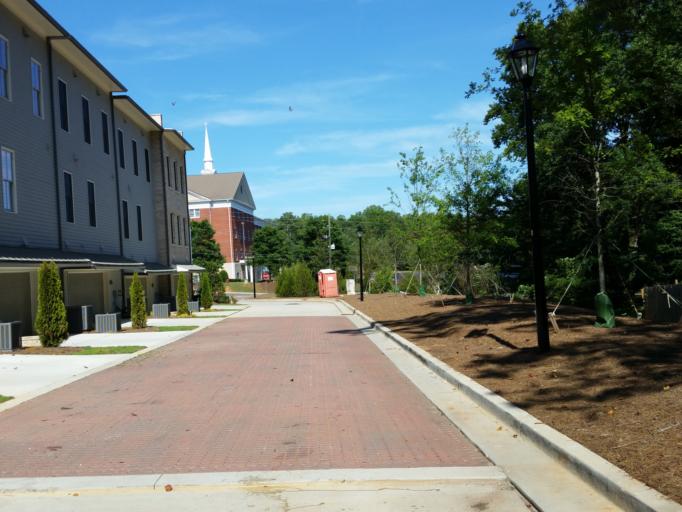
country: US
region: Georgia
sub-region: Fulton County
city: Roswell
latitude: 34.0222
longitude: -84.3570
